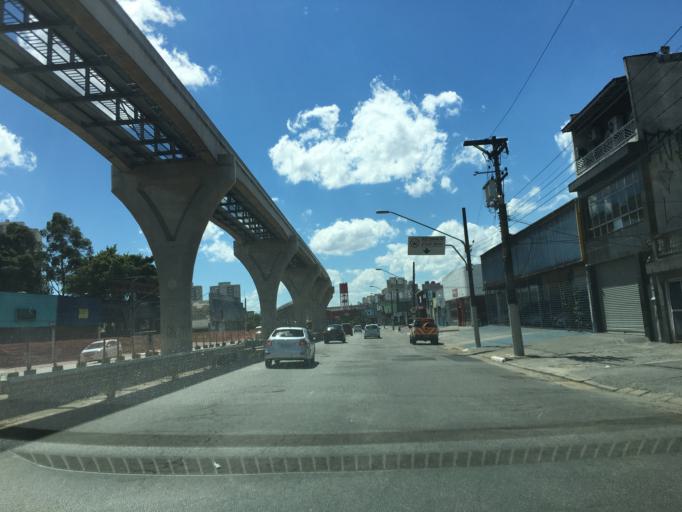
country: BR
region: Sao Paulo
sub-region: Sao Caetano Do Sul
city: Sao Caetano do Sul
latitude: -23.5835
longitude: -46.5514
